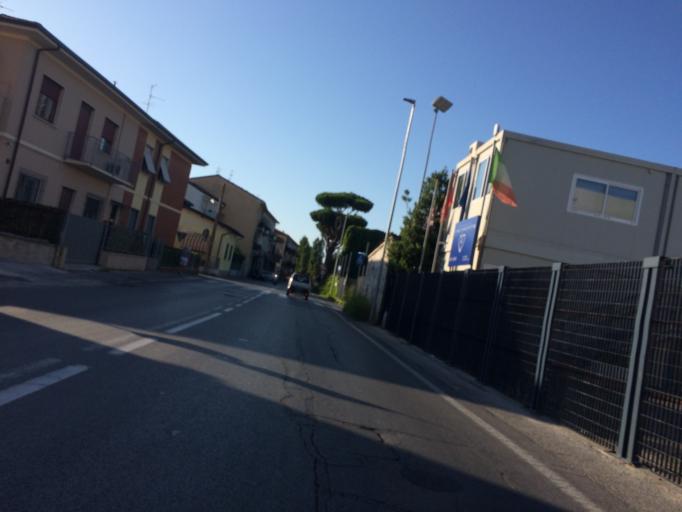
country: IT
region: Tuscany
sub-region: Provincia di Lucca
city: Viareggio
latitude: 43.8633
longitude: 10.2588
